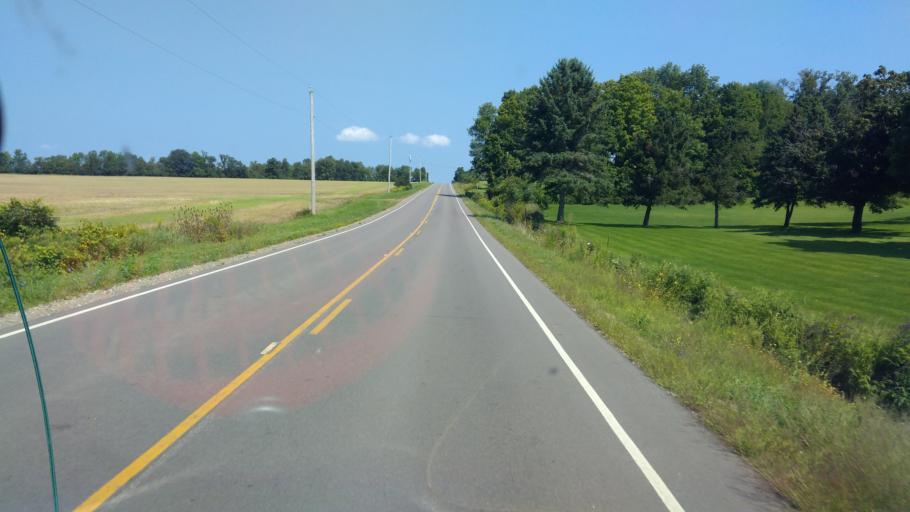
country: US
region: New York
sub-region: Allegany County
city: Belmont
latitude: 42.2500
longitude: -78.0402
